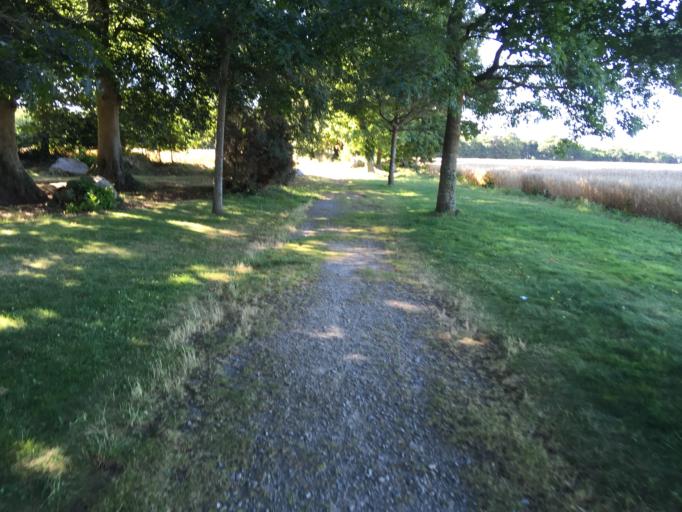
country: FR
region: Brittany
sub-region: Departement des Cotes-d'Armor
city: Pleslin-Trigavou
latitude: 48.5293
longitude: -2.0587
